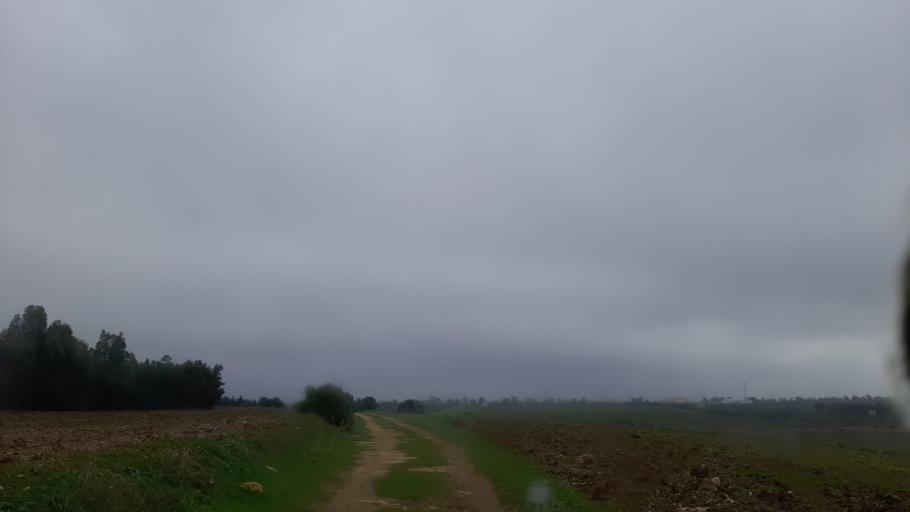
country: TN
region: Nabul
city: Qulaybiyah
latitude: 36.8285
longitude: 11.0338
